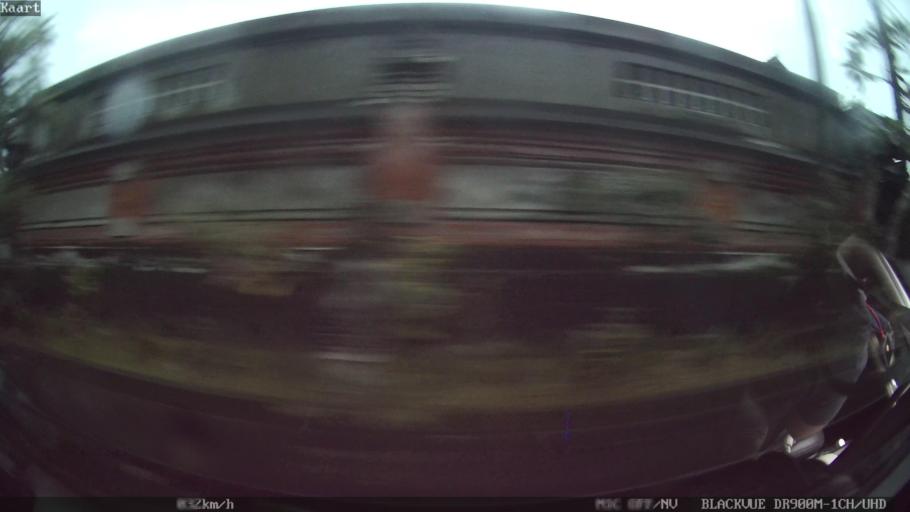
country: ID
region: Bali
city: Banjar Sedang
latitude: -8.5581
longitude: 115.2515
